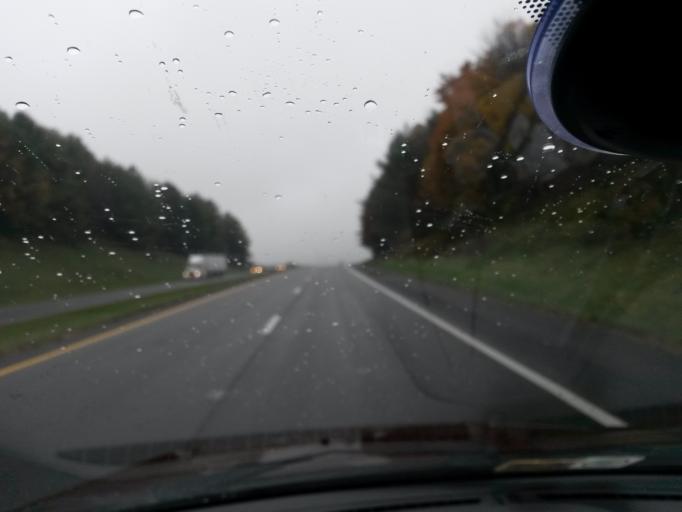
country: US
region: Virginia
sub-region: Montgomery County
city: Christiansburg
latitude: 37.1399
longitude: -80.3830
